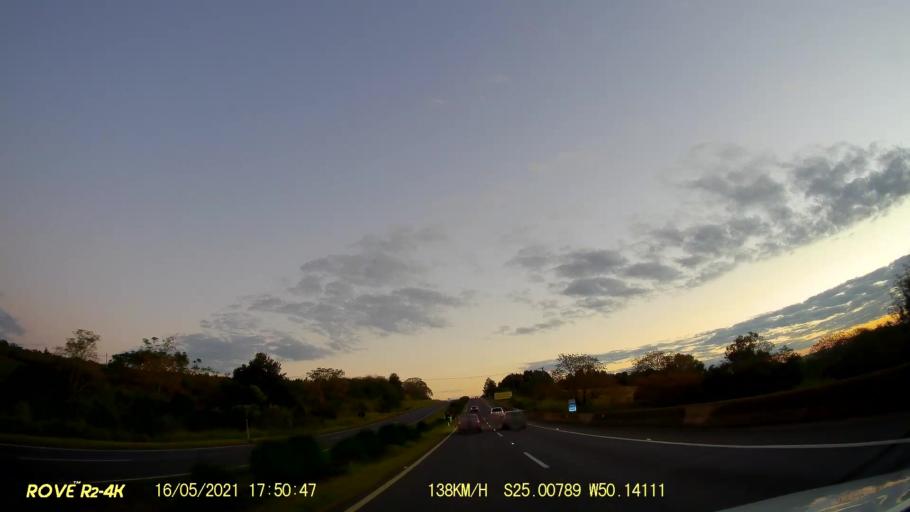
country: BR
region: Parana
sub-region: Carambei
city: Carambei
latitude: -25.0079
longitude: -50.1411
